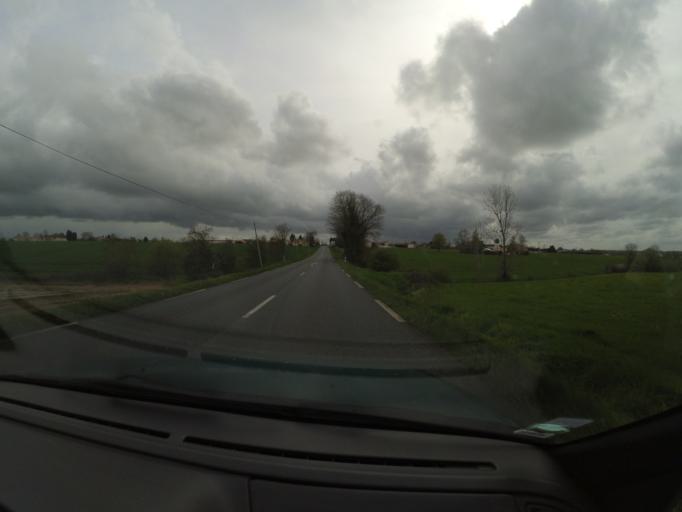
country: FR
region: Pays de la Loire
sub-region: Departement de la Loire-Atlantique
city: La Remaudiere
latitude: 47.2424
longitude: -1.2128
